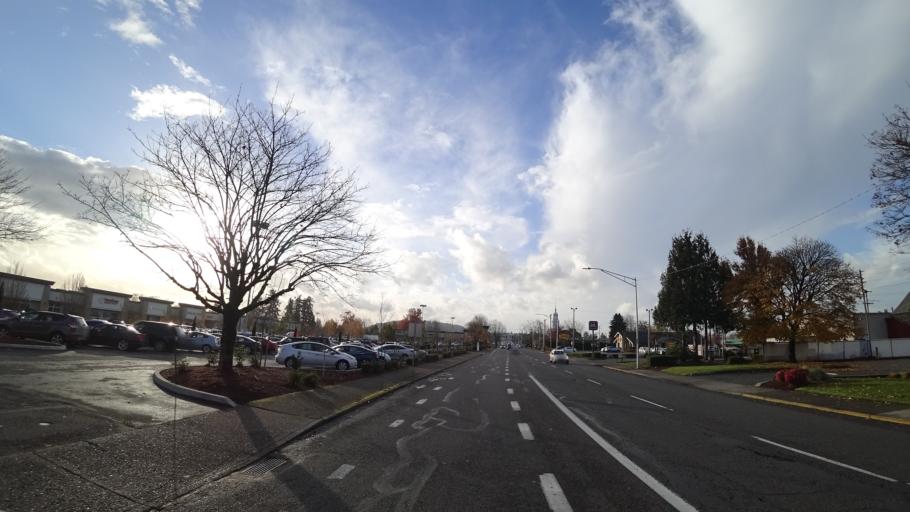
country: US
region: Oregon
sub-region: Multnomah County
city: Lents
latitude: 45.5183
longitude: -122.5549
